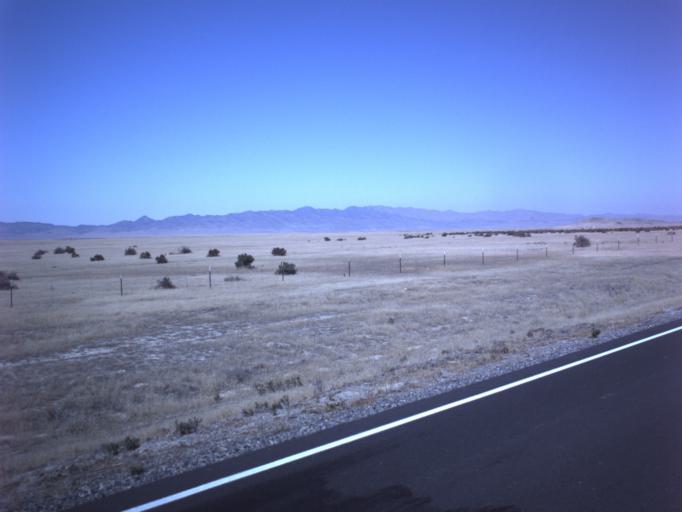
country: US
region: Utah
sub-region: Tooele County
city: Grantsville
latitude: 40.3170
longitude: -112.7436
